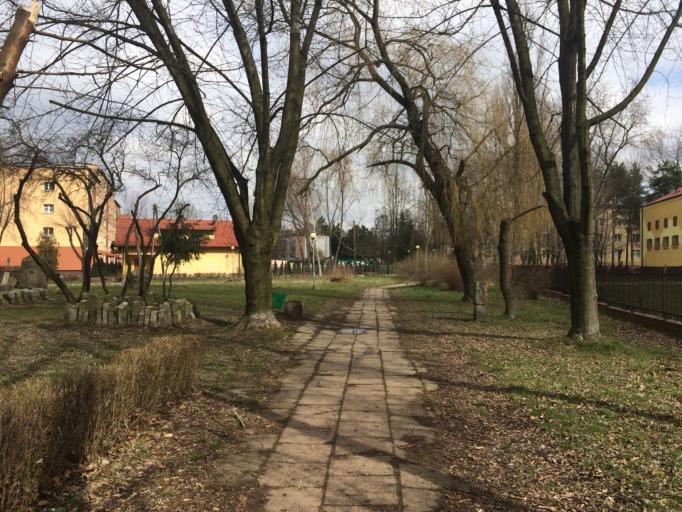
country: PL
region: Swietokrzyskie
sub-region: Powiat starachowicki
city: Starachowice
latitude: 51.0538
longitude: 21.0746
